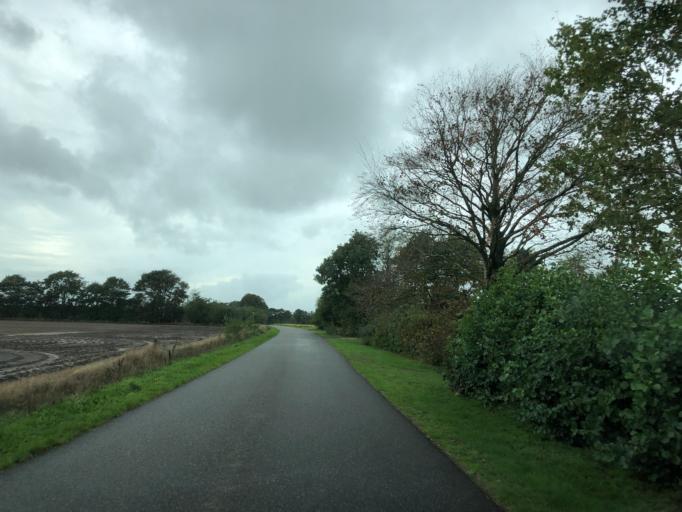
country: DK
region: Central Jutland
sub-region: Herning Kommune
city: Vildbjerg
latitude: 56.1953
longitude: 8.8093
